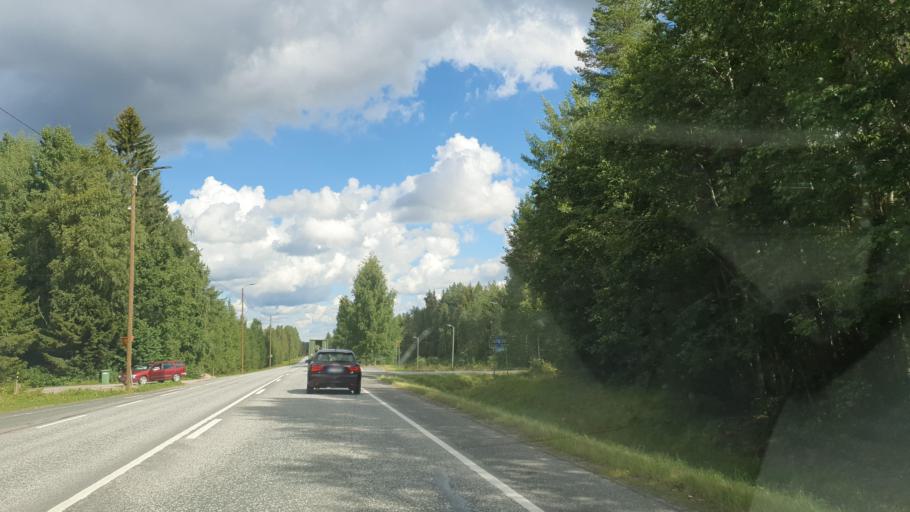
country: FI
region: Kainuu
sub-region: Kajaani
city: Kajaani
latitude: 64.2001
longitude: 27.6361
